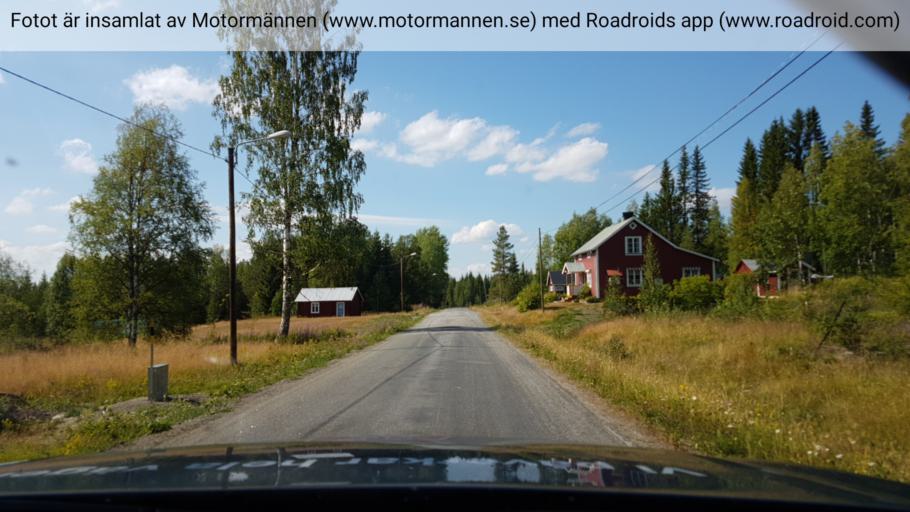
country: SE
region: Vaesterbotten
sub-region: Dorotea Kommun
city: Dorotea
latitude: 64.1035
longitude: 16.3898
